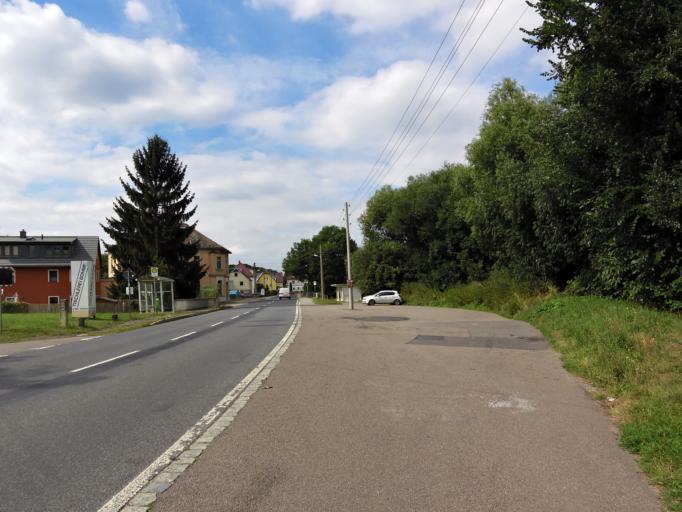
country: DE
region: Saxony
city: Coswig
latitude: 51.1100
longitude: 13.5697
